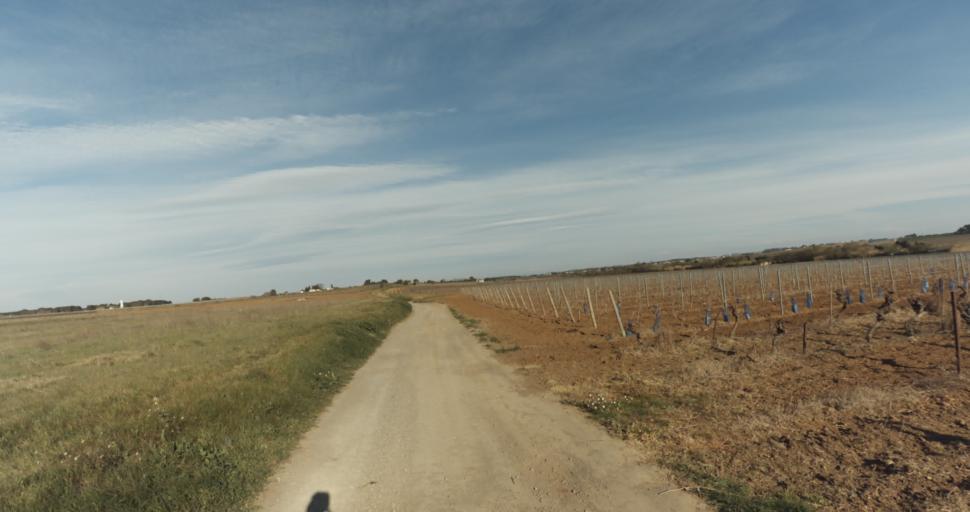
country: FR
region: Languedoc-Roussillon
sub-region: Departement de l'Herault
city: Marseillan
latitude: 43.3678
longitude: 3.5173
